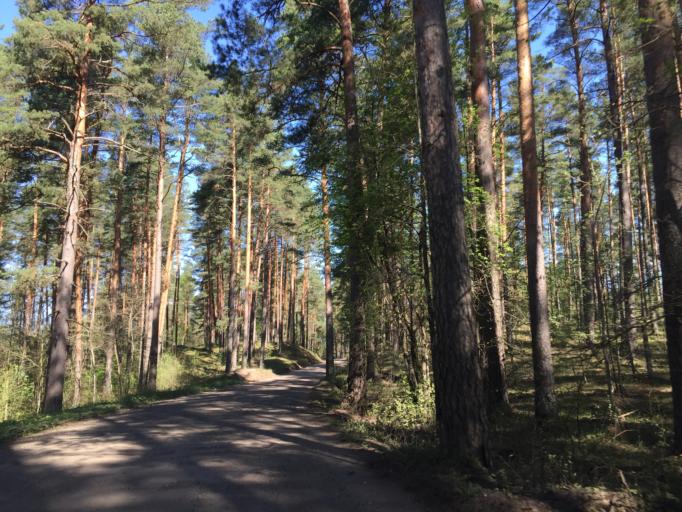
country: LV
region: Adazi
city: Adazi
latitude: 57.0894
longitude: 24.3414
